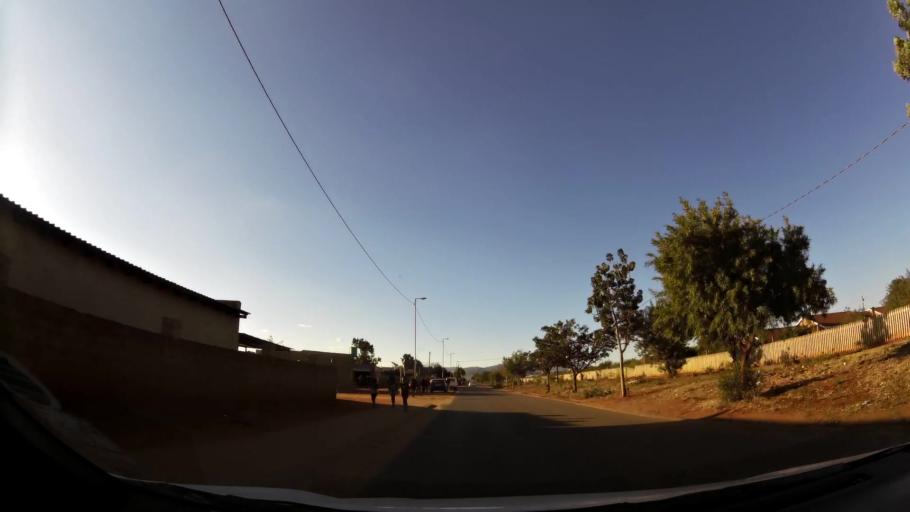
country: ZA
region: Limpopo
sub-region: Waterberg District Municipality
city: Mokopane
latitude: -24.1533
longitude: 28.9859
